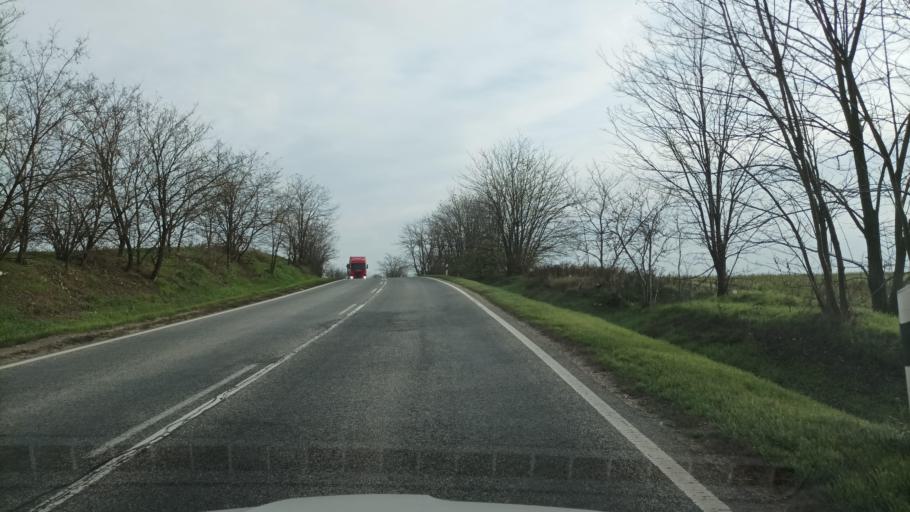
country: HU
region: Pest
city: Alsonemedi
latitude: 47.3240
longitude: 19.1925
